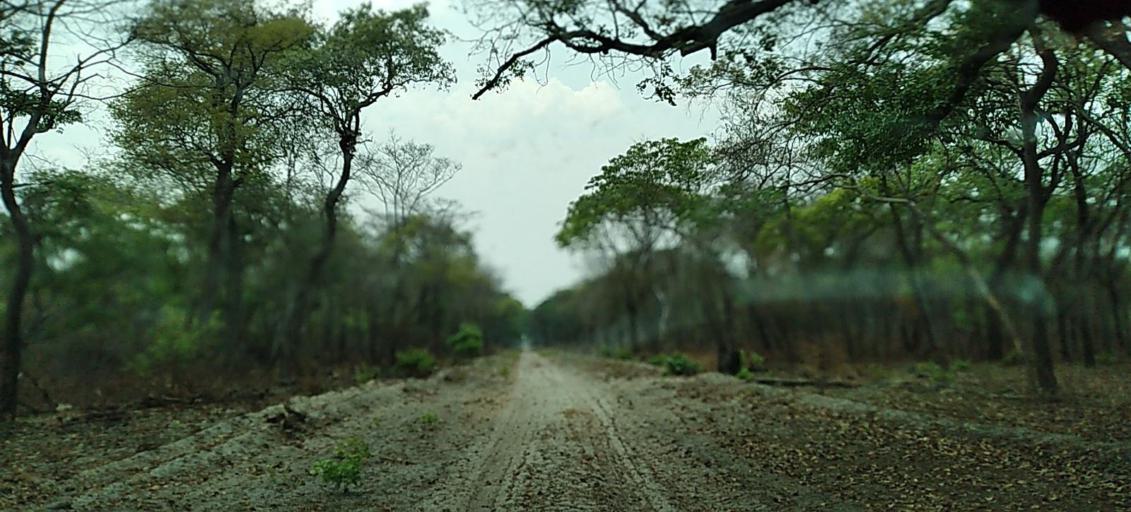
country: ZM
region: Western
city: Lukulu
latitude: -14.0174
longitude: 23.5792
